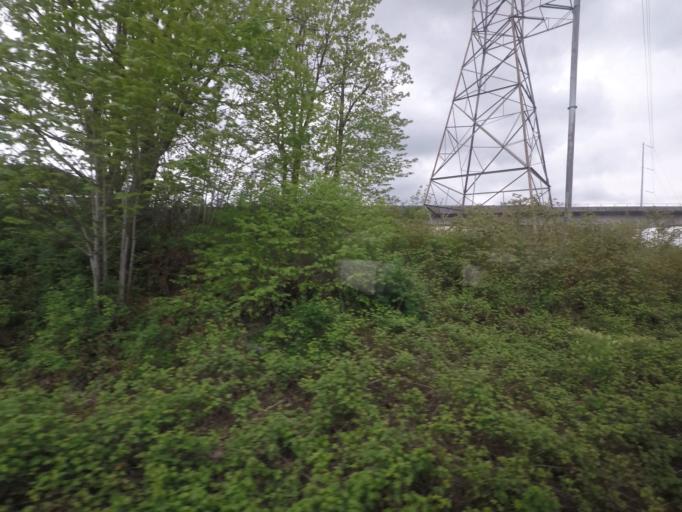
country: CA
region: British Columbia
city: New Westminster
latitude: 49.2343
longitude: -122.8821
